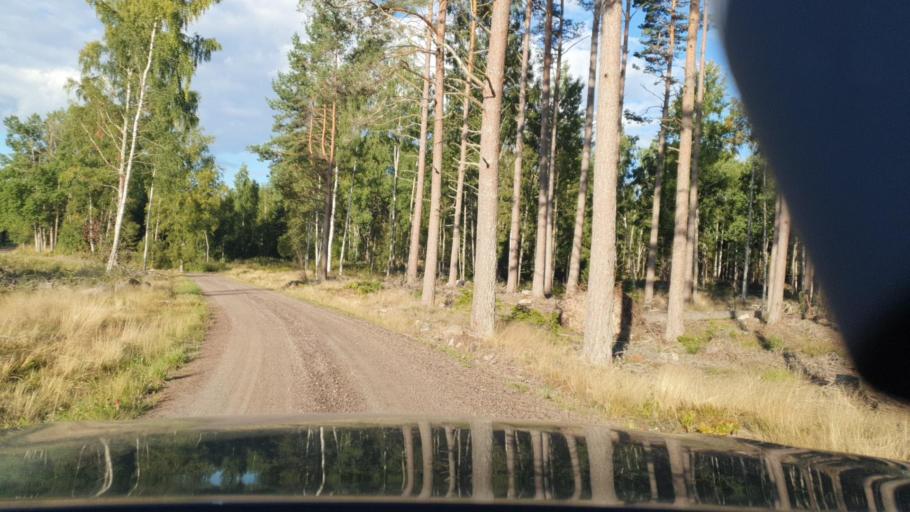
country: SE
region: Vaermland
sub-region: Kristinehamns Kommun
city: Kristinehamn
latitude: 59.1586
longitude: 14.0984
